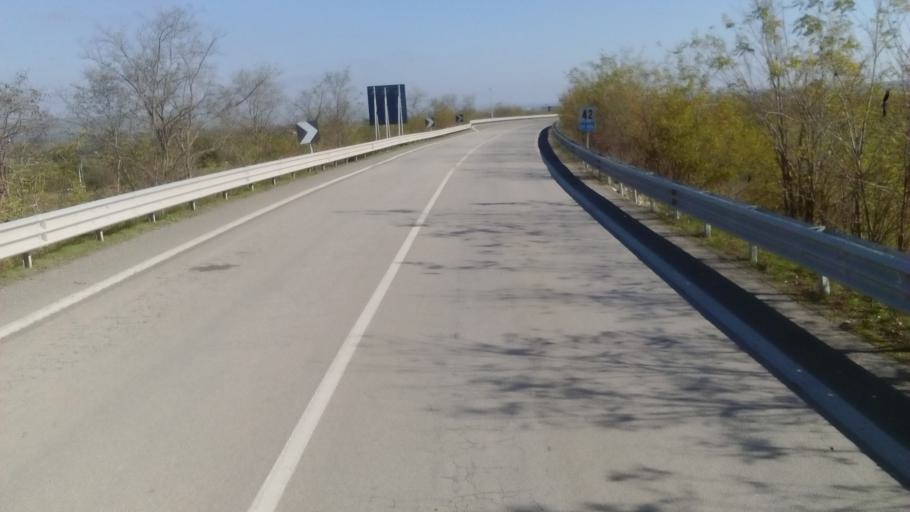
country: IT
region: Basilicate
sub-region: Provincia di Potenza
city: Zona 179
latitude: 41.0825
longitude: 15.6206
